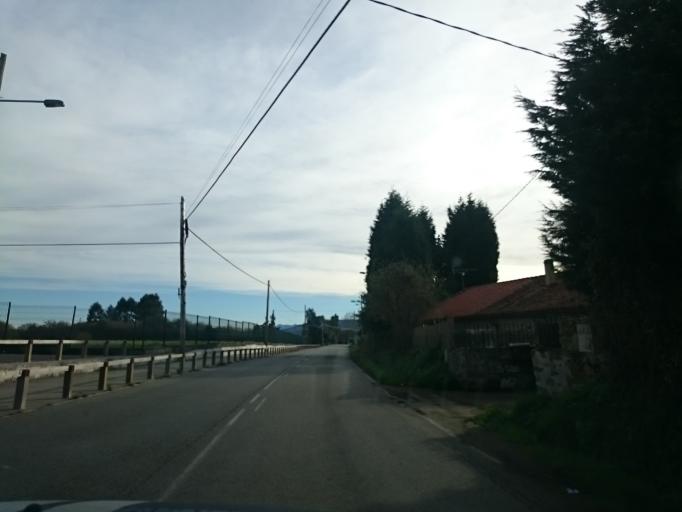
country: ES
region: Asturias
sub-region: Province of Asturias
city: Gijon
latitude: 43.5128
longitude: -5.6039
